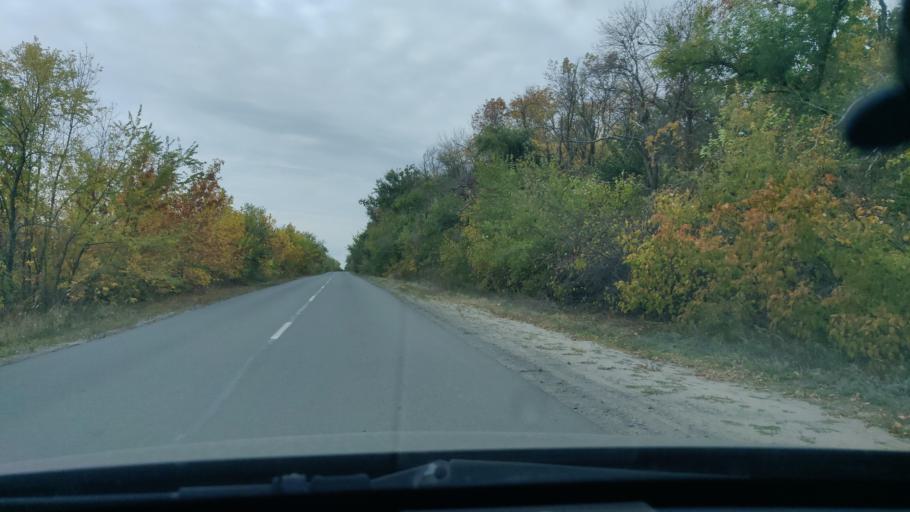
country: RU
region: Rostov
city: Ust'-Donetskiy
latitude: 47.6518
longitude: 40.8918
